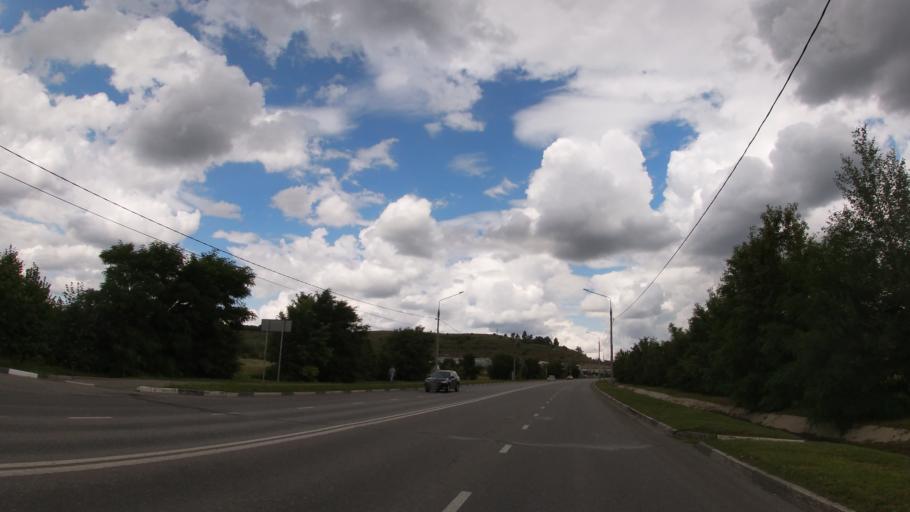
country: RU
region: Belgorod
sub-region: Belgorodskiy Rayon
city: Belgorod
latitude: 50.6125
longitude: 36.6127
